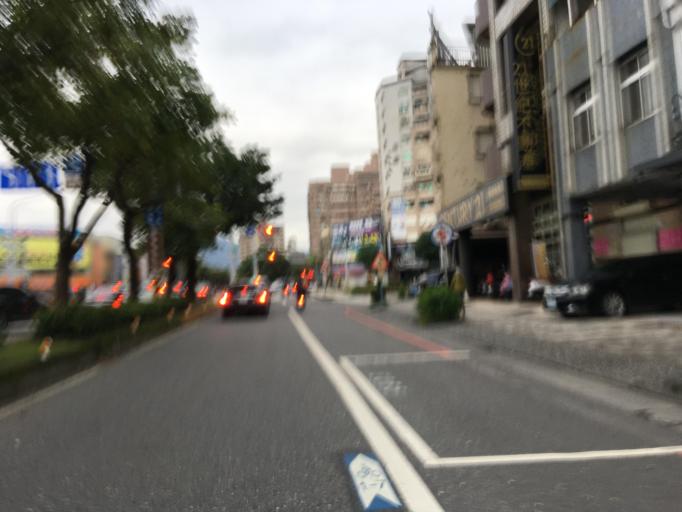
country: TW
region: Taiwan
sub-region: Yilan
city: Yilan
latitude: 24.6807
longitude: 121.7642
